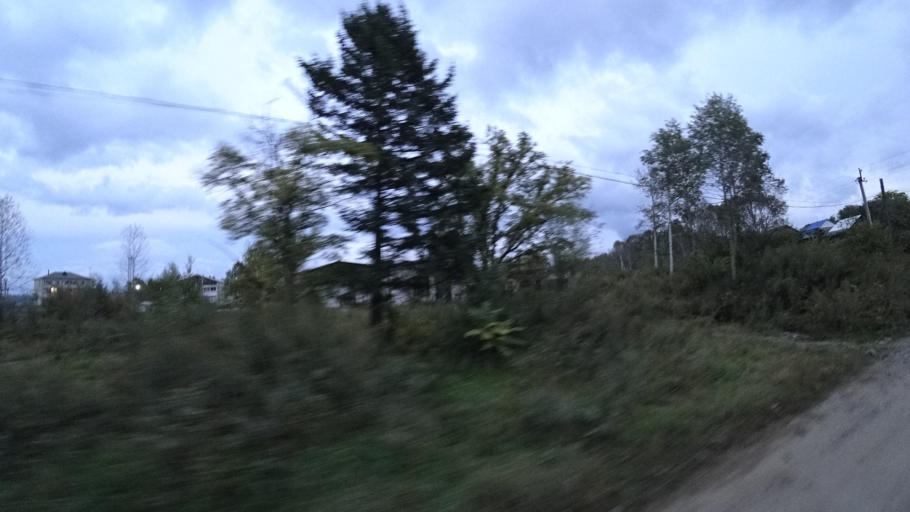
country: RU
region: Jewish Autonomous Oblast
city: Izvestkovyy
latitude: 48.9816
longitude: 131.5553
